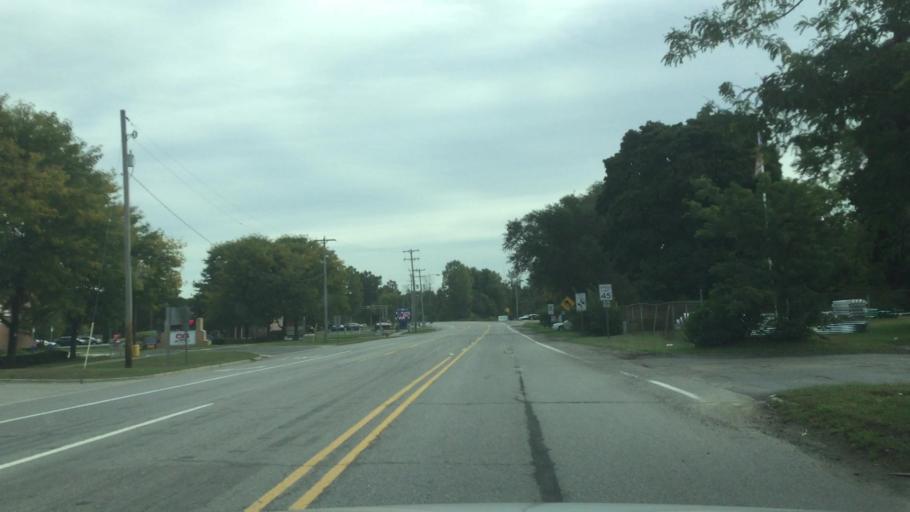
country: US
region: Michigan
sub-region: Oakland County
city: Holly
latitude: 42.8064
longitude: -83.6277
